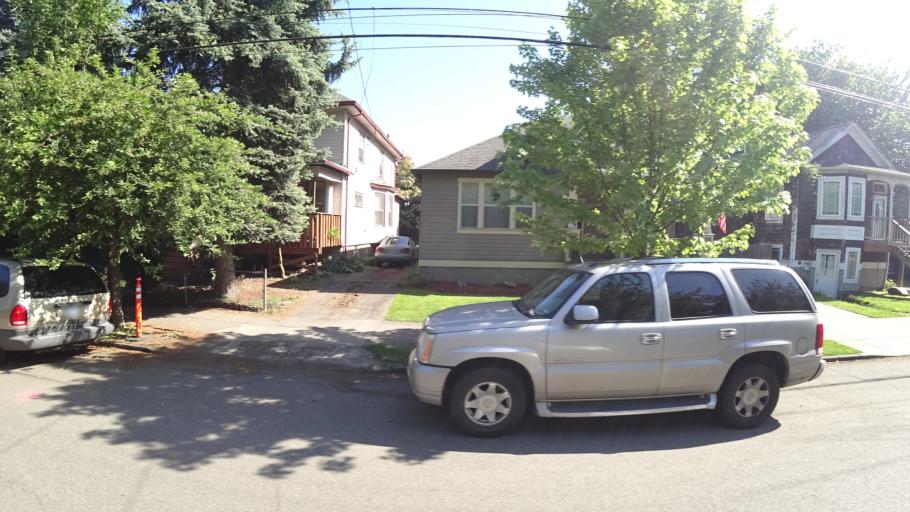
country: US
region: Oregon
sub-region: Multnomah County
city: Portland
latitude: 45.5380
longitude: -122.6630
